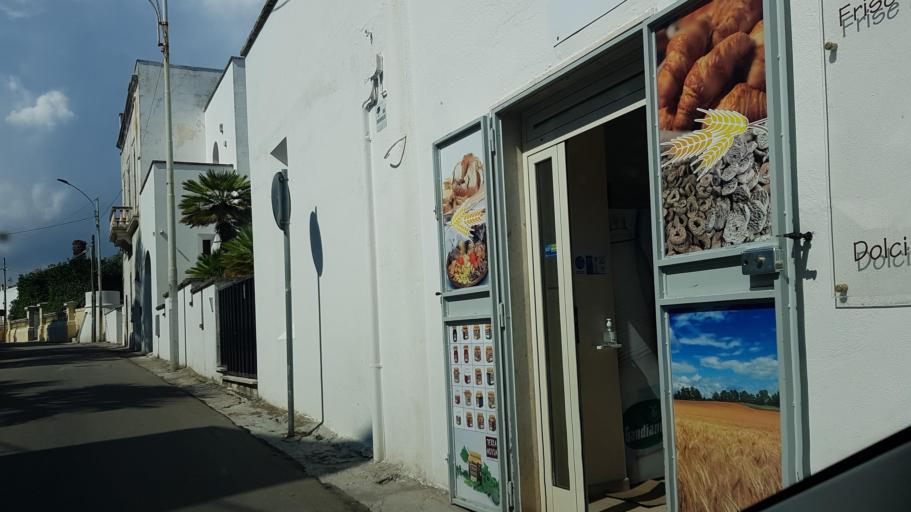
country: IT
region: Apulia
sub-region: Provincia di Lecce
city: Leuca
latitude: 39.7982
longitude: 18.3587
